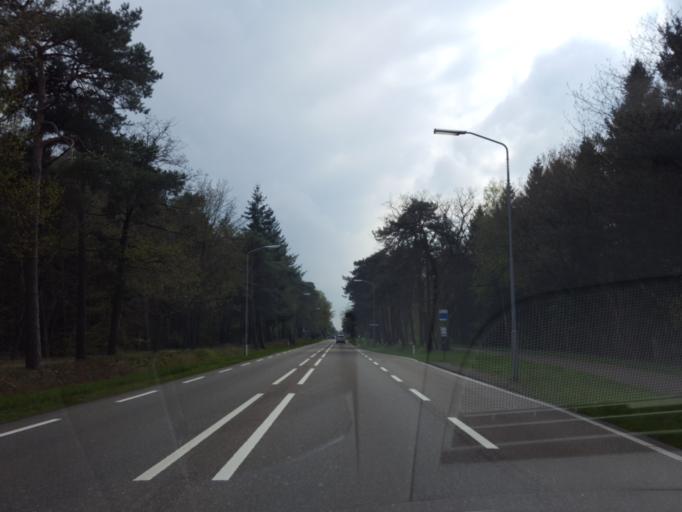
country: NL
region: North Brabant
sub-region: Gemeente Valkenswaard
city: Valkenswaard
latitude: 51.3701
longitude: 5.4664
